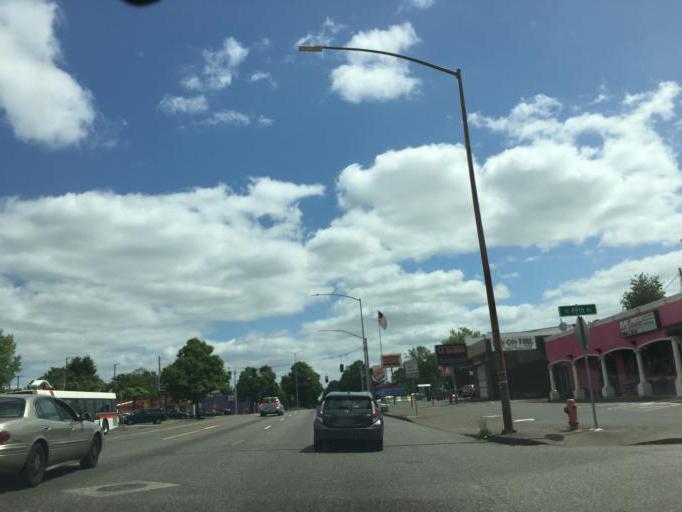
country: US
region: Oregon
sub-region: Multnomah County
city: Lents
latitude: 45.4975
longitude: -122.6128
